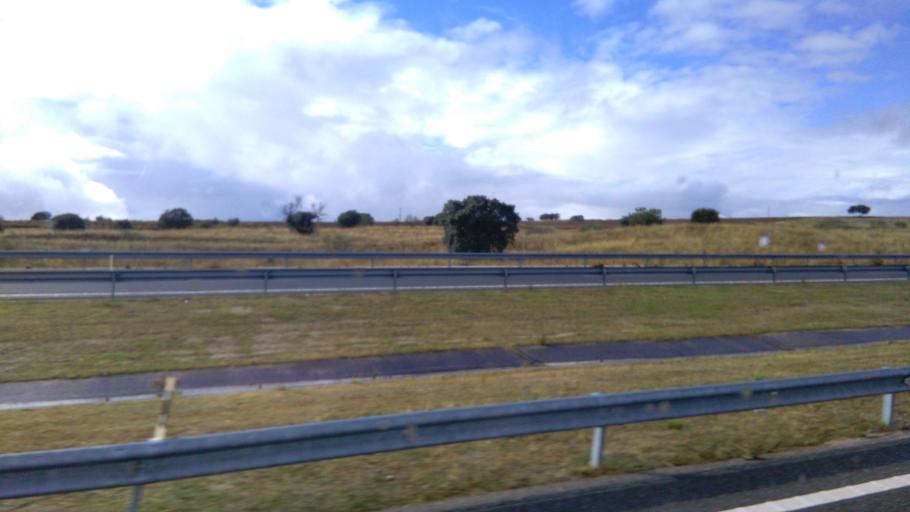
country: ES
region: Madrid
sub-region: Provincia de Madrid
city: El Alamo
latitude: 40.2611
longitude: -3.9921
